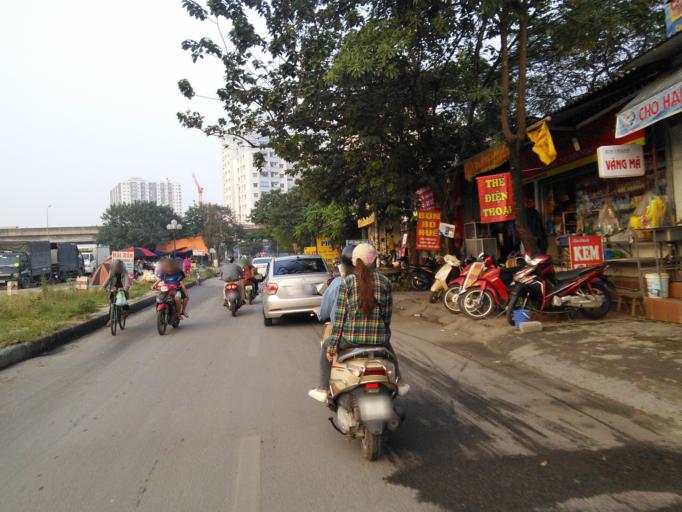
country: VN
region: Ha Noi
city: Van Dien
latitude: 20.9695
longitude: 105.8249
